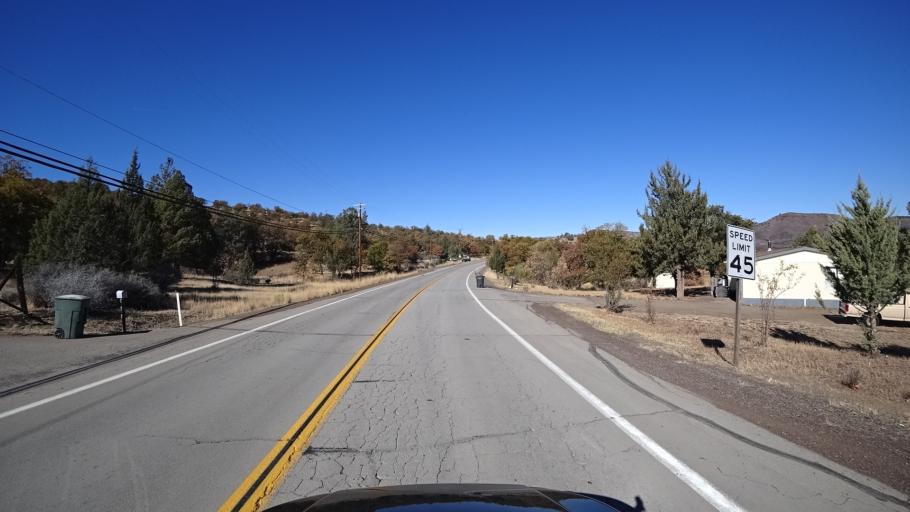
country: US
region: California
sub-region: Siskiyou County
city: Montague
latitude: 41.8869
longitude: -122.4906
